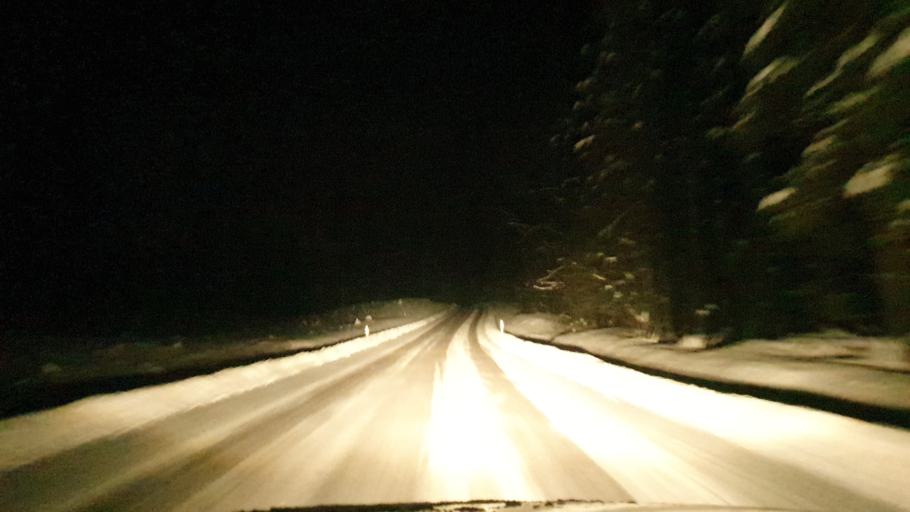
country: EE
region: Vorumaa
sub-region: Antsla vald
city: Vana-Antsla
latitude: 57.9721
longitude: 26.7594
